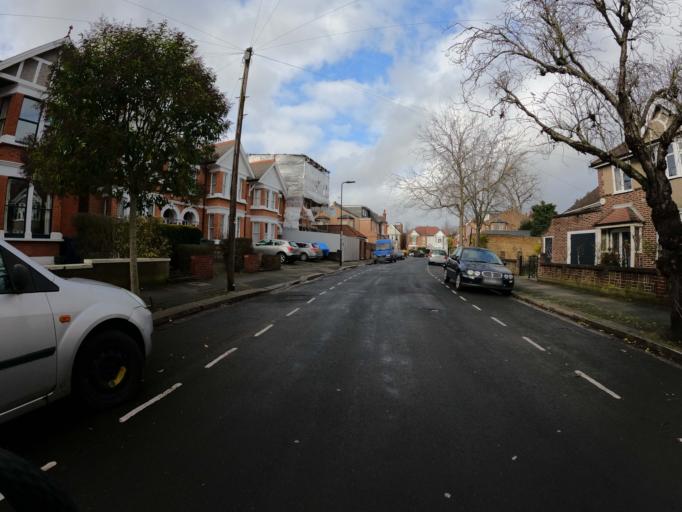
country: GB
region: England
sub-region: Greater London
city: Acton
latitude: 51.5105
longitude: -0.2753
